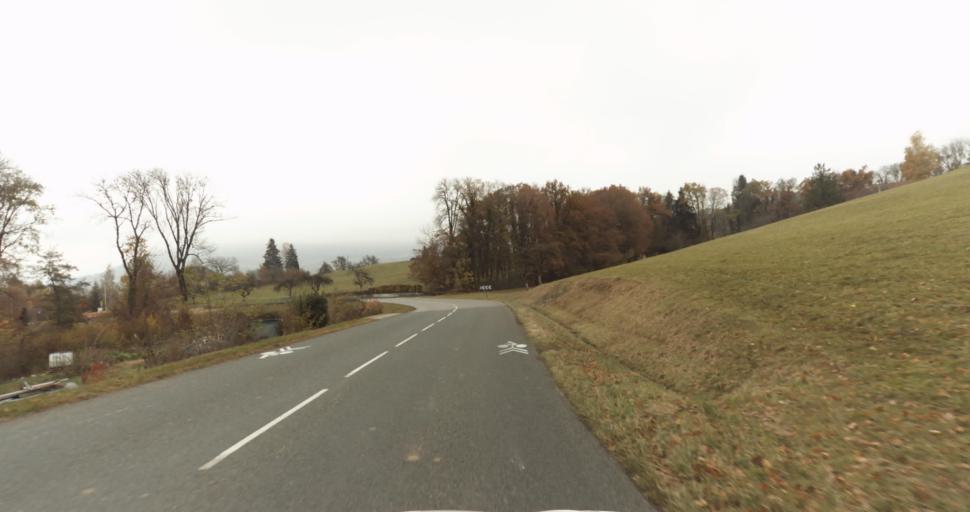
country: FR
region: Rhone-Alpes
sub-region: Departement de la Haute-Savoie
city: Cusy
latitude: 45.7784
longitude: 6.0167
